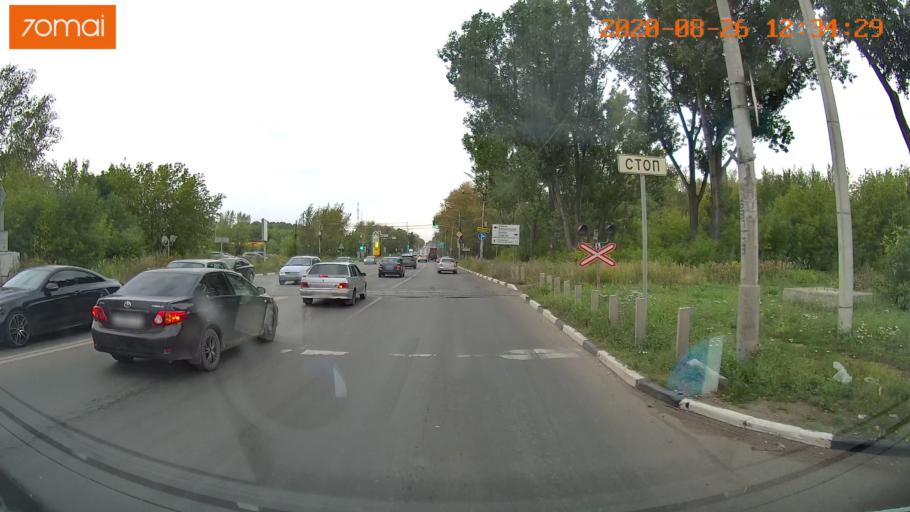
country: RU
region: Rjazan
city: Ryazan'
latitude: 54.5886
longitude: 39.7712
